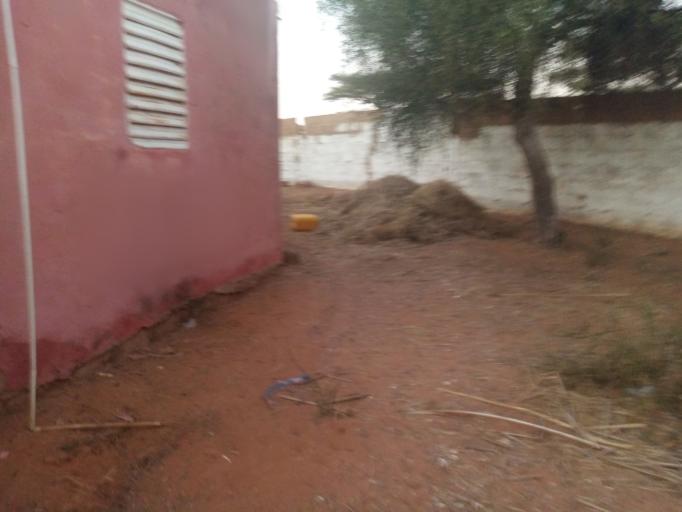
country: SN
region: Saint-Louis
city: Saint-Louis
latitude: 15.9723
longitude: -16.3710
